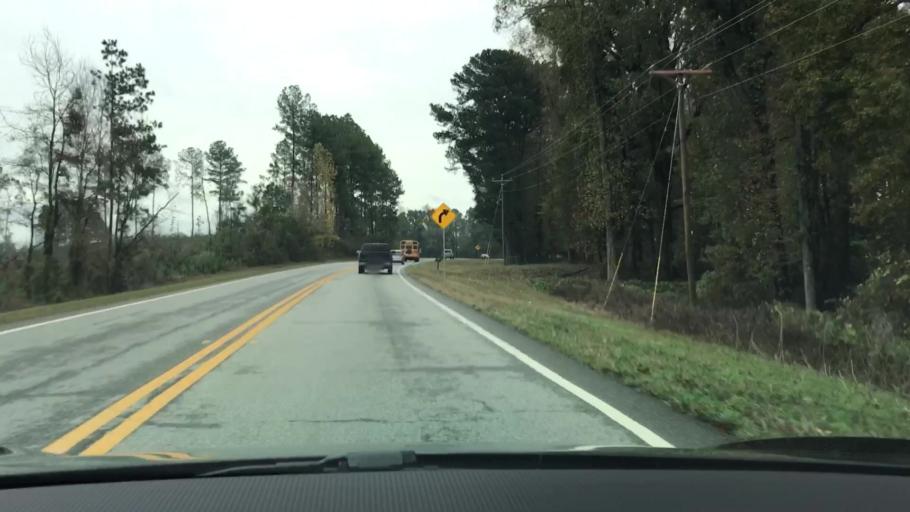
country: US
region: Georgia
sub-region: Greene County
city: Greensboro
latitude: 33.6068
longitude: -83.2005
